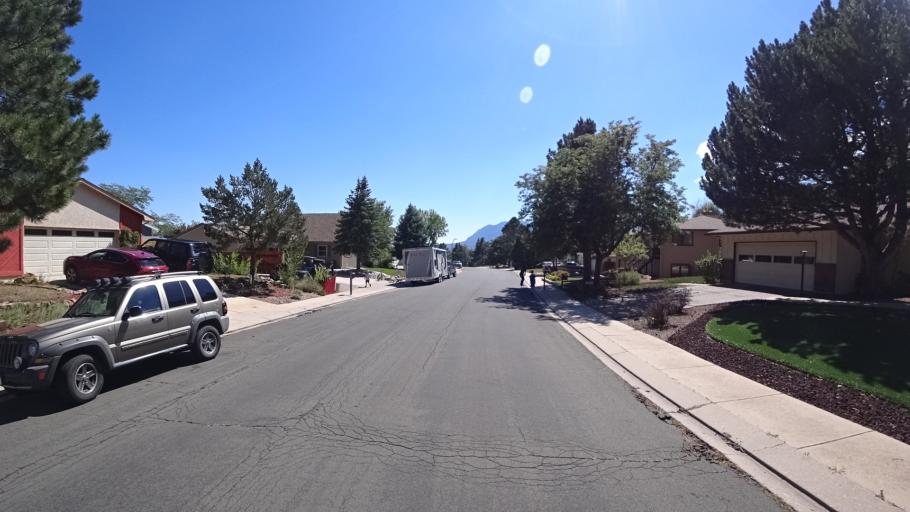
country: US
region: Colorado
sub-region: El Paso County
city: Colorado Springs
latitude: 38.8585
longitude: -104.8543
